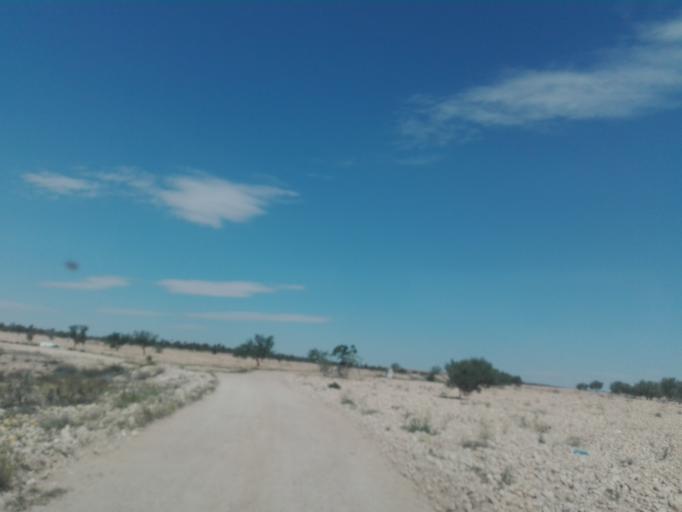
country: TN
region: Safaqis
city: Sfax
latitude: 34.6889
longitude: 10.5312
